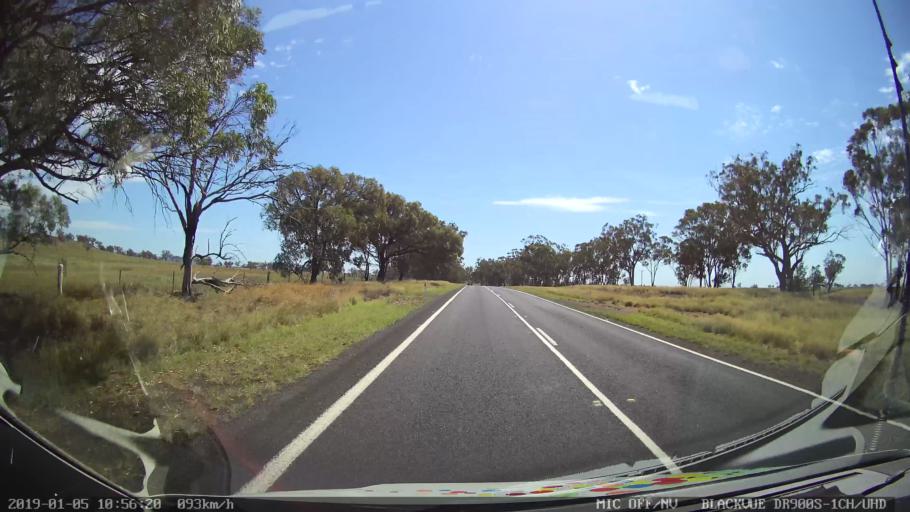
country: AU
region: New South Wales
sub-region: Warrumbungle Shire
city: Coonabarabran
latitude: -31.4422
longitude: 149.1568
